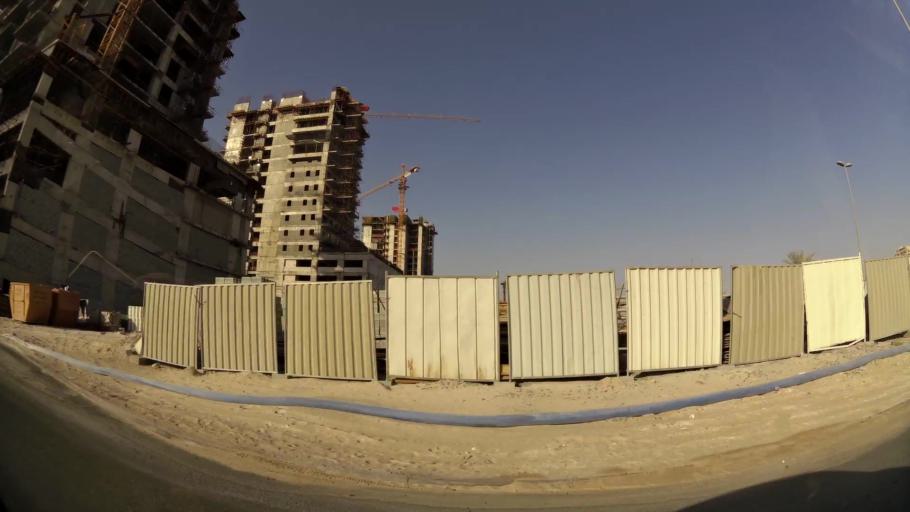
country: AE
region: Dubai
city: Dubai
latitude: 25.0598
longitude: 55.2157
